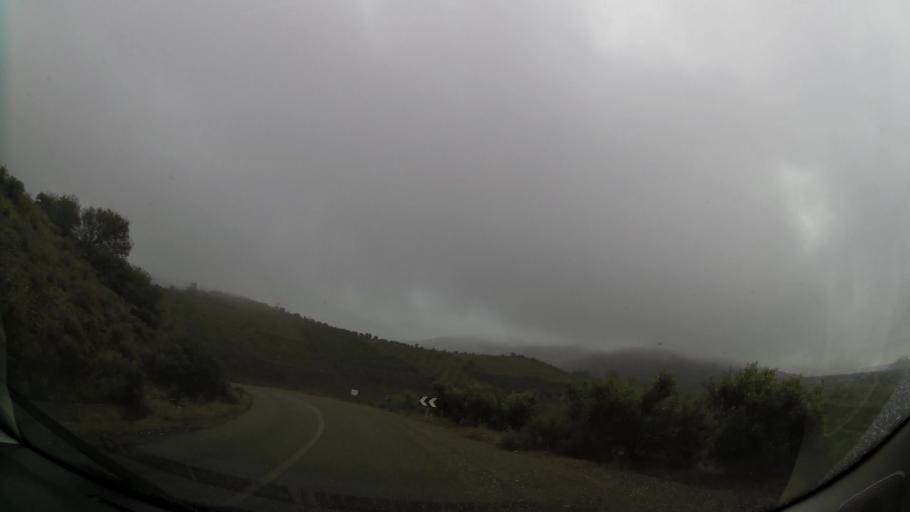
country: MA
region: Taza-Al Hoceima-Taounate
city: Imzourene
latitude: 35.1192
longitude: -3.7780
